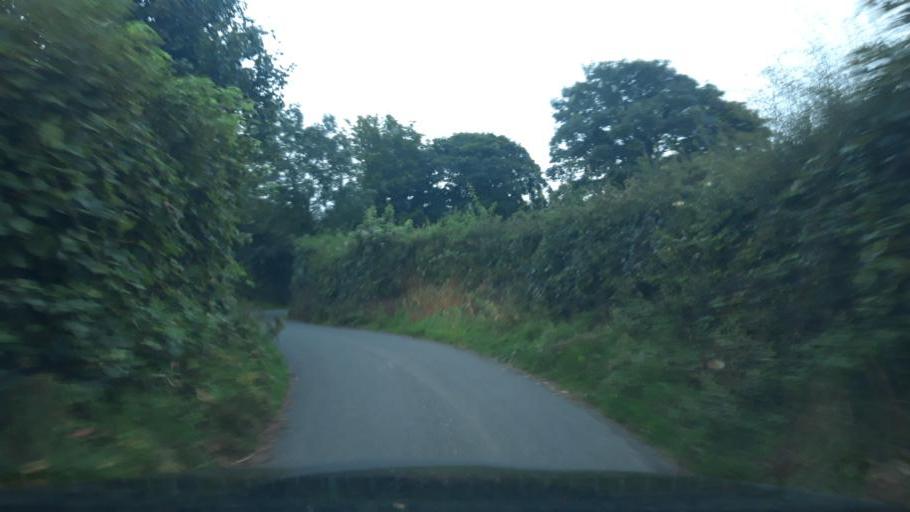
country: IE
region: Leinster
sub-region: Kilkenny
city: Graiguenamanagh
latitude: 52.5779
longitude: -7.0304
